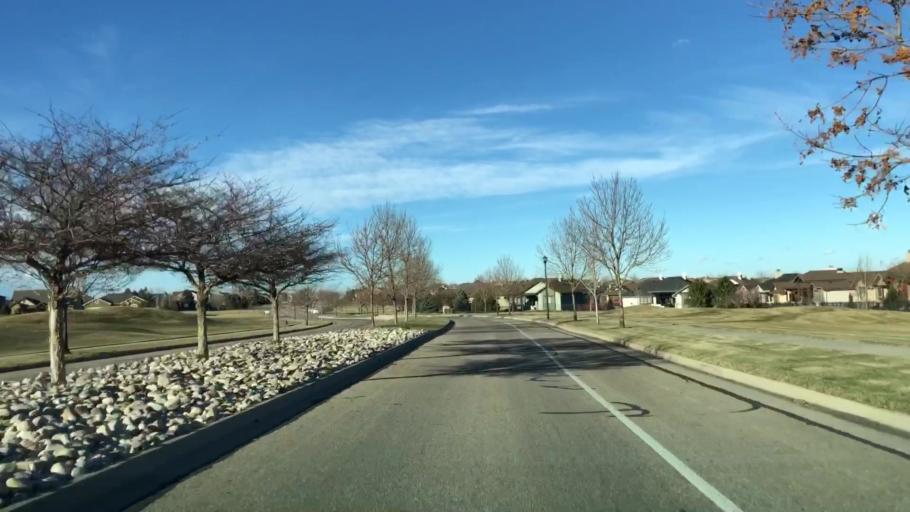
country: US
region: Colorado
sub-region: Weld County
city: Windsor
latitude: 40.4590
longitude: -104.9764
